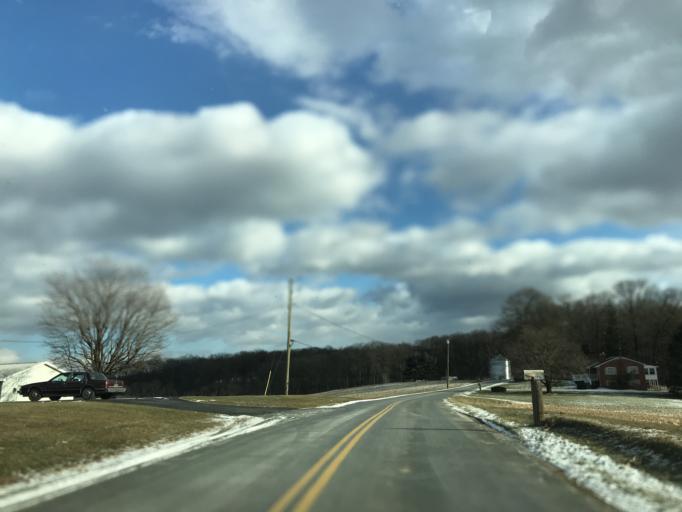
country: US
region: Maryland
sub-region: Harford County
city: Jarrettsville
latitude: 39.6423
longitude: -76.4935
